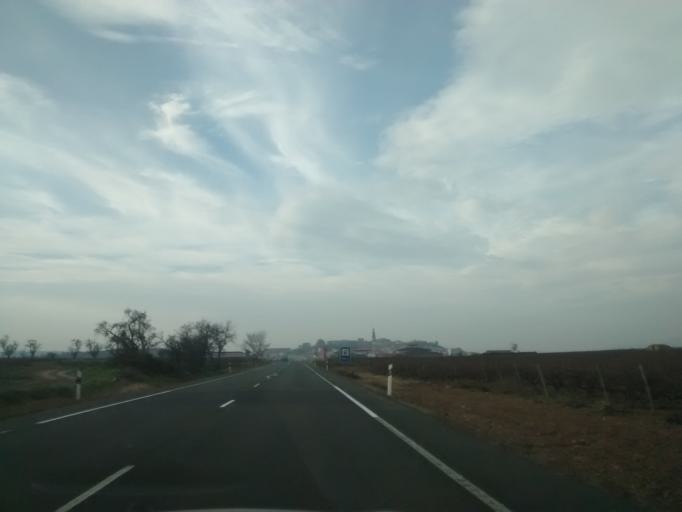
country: ES
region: La Rioja
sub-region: Provincia de La Rioja
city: Briones
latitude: 42.5341
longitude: -2.7685
